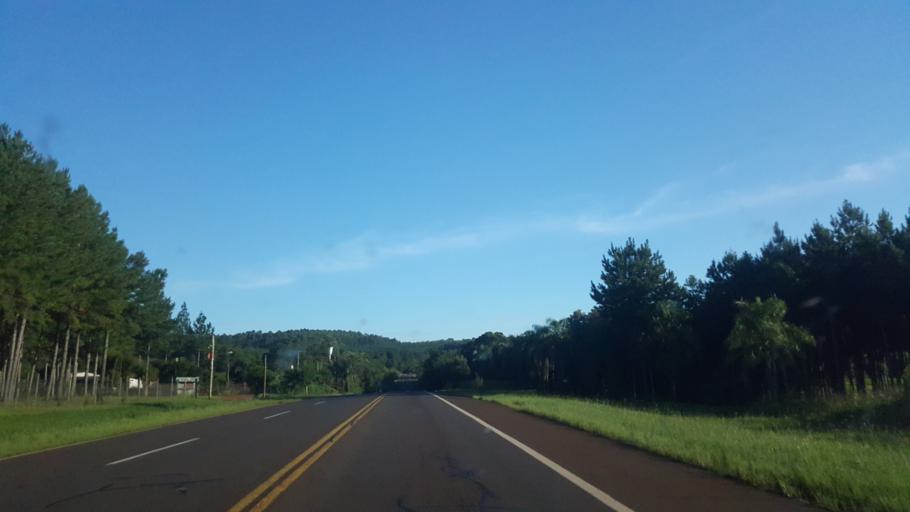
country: AR
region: Misiones
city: Caraguatay
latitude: -26.6542
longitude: -54.7539
